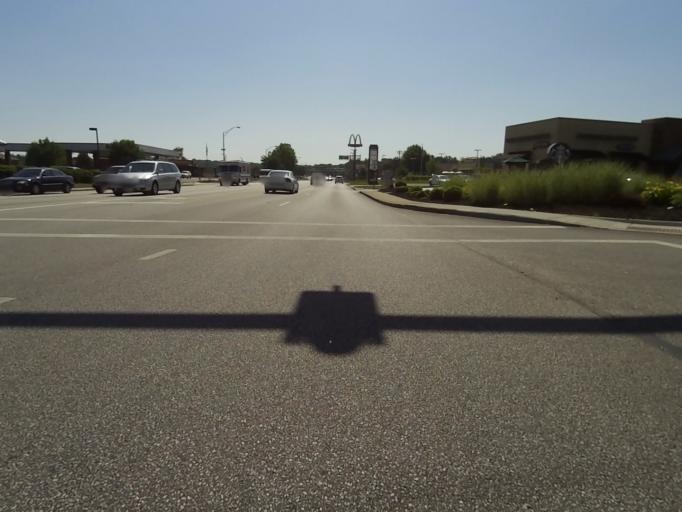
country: US
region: Ohio
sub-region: Summit County
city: Silver Lake
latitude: 41.1635
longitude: -81.4770
